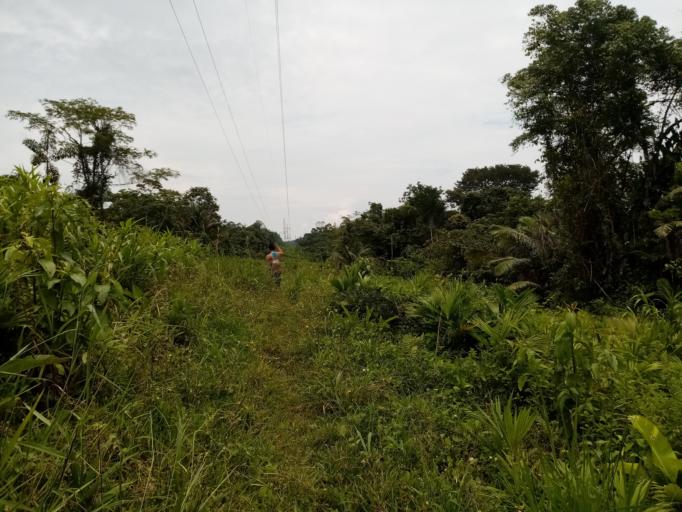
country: EC
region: Napo
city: Tena
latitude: -0.9694
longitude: -77.7974
